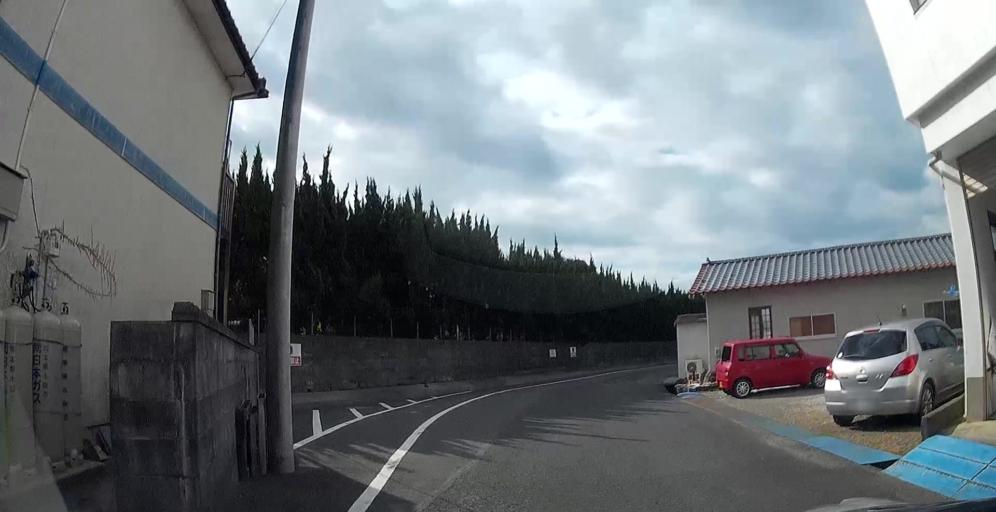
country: JP
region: Kumamoto
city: Minamata
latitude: 32.2114
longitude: 130.3912
